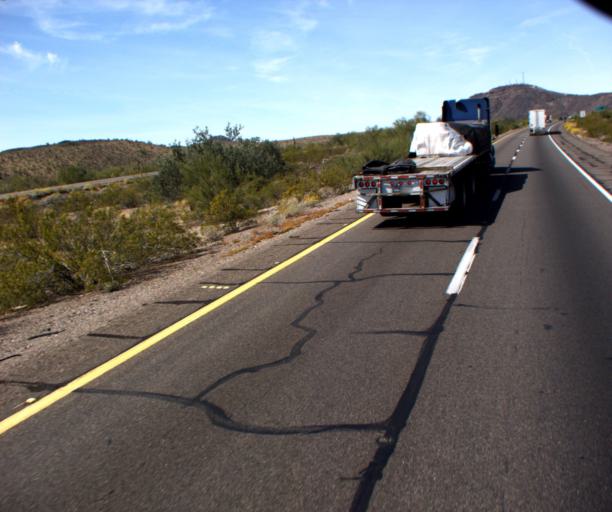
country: US
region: Arizona
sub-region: La Paz County
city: Quartzsite
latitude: 33.6639
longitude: -114.0264
